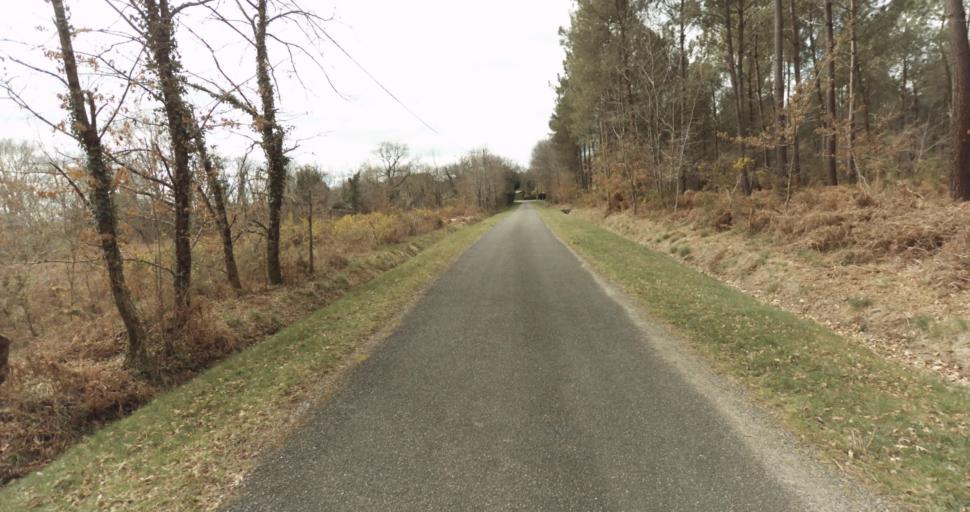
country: FR
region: Aquitaine
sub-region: Departement des Landes
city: Roquefort
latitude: 44.0710
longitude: -0.3947
